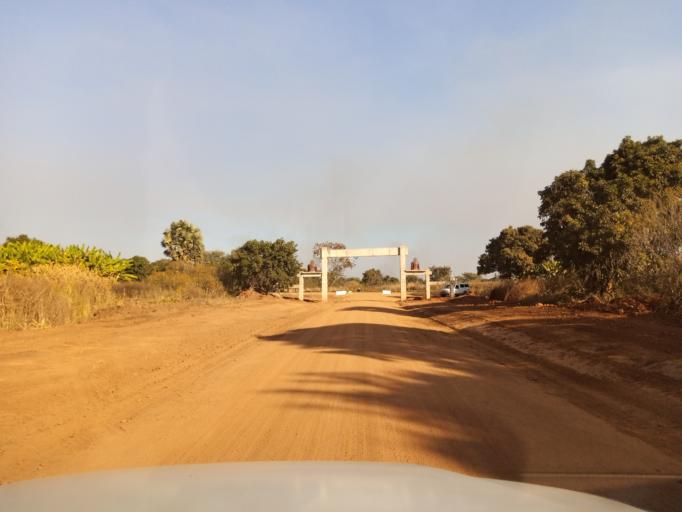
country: CD
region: Katanga
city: Lubumbashi
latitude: -11.3092
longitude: 27.2846
